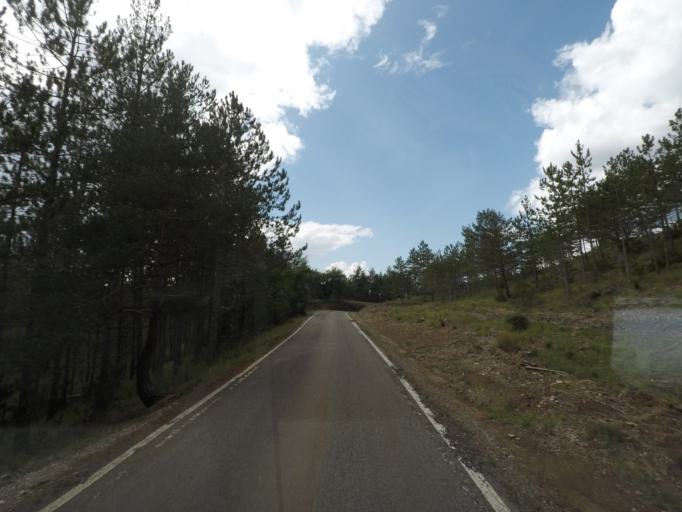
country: ES
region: Aragon
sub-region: Provincia de Huesca
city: Fiscal
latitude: 42.4084
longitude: -0.1532
